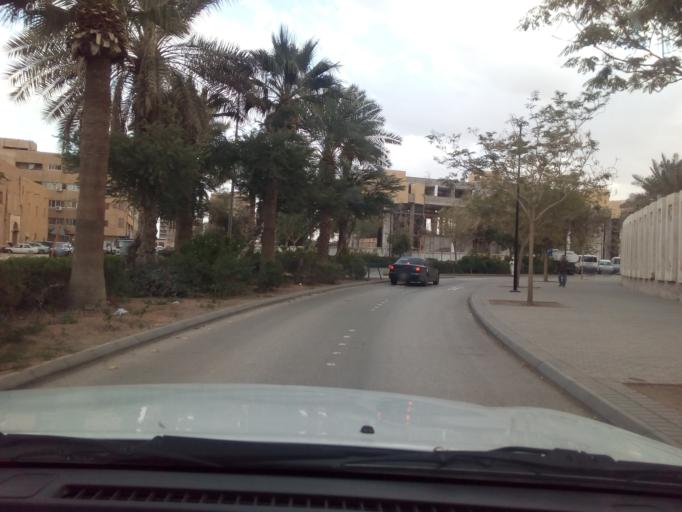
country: SA
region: Ar Riyad
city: Riyadh
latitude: 24.6418
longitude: 46.7098
